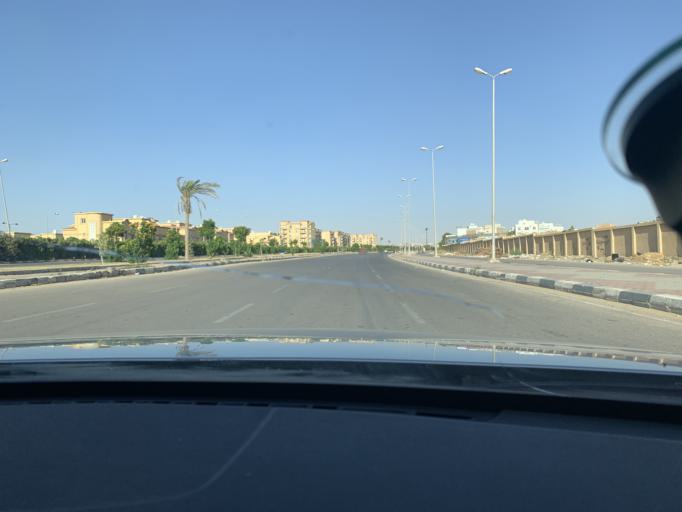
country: EG
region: Muhafazat al Qalyubiyah
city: Al Khankah
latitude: 30.0531
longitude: 31.5023
